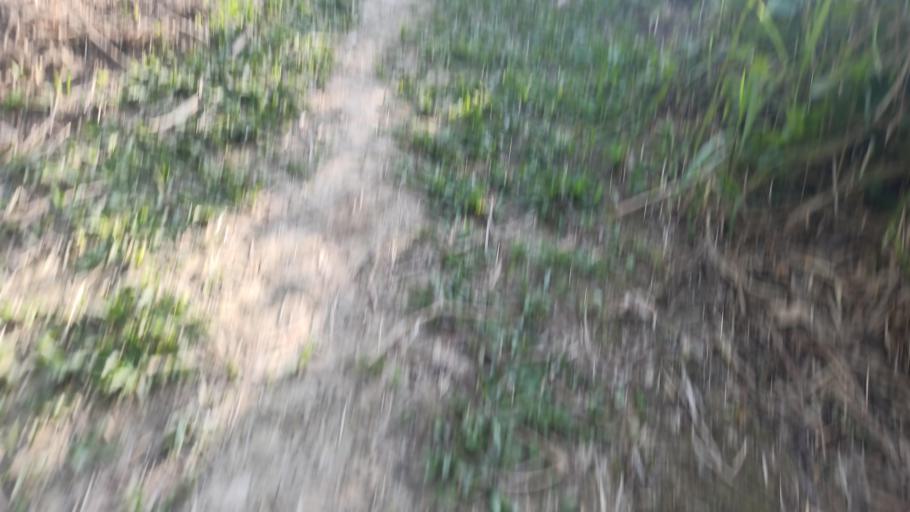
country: MX
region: Veracruz
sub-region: Poza Rica de Hidalgo
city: Arroyo del Maiz Uno
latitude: 20.4835
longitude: -97.3832
